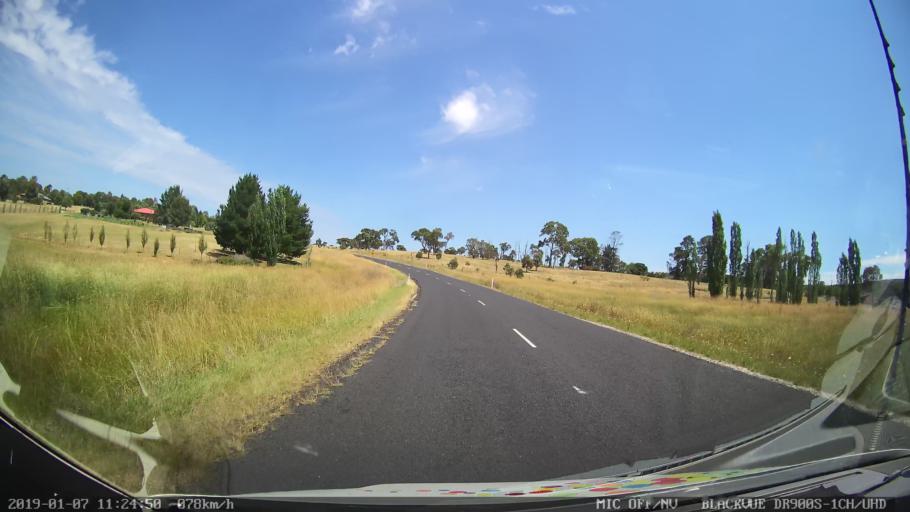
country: AU
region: New South Wales
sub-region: Armidale Dumaresq
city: Armidale
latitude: -30.4624
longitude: 151.6088
